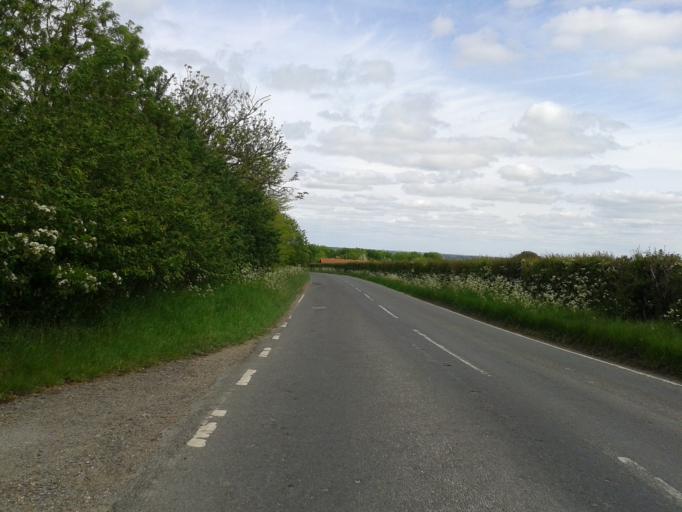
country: GB
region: England
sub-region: Cambridgeshire
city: Haslingfield
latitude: 52.1445
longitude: 0.0474
